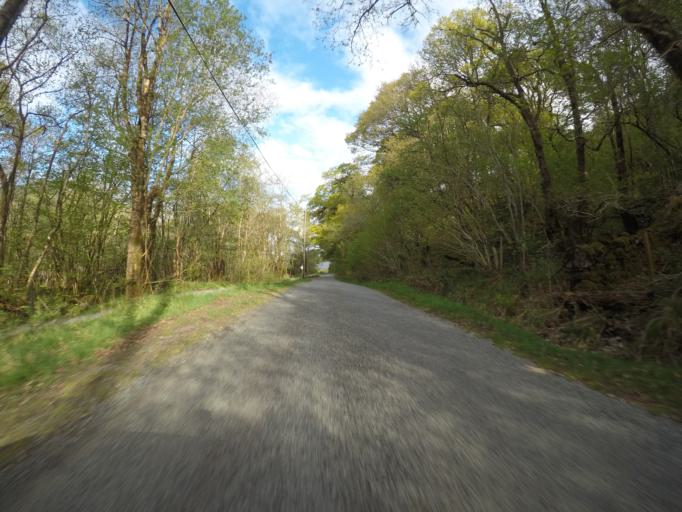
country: GB
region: Scotland
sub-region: Highland
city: Fort William
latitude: 56.6762
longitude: -5.0779
